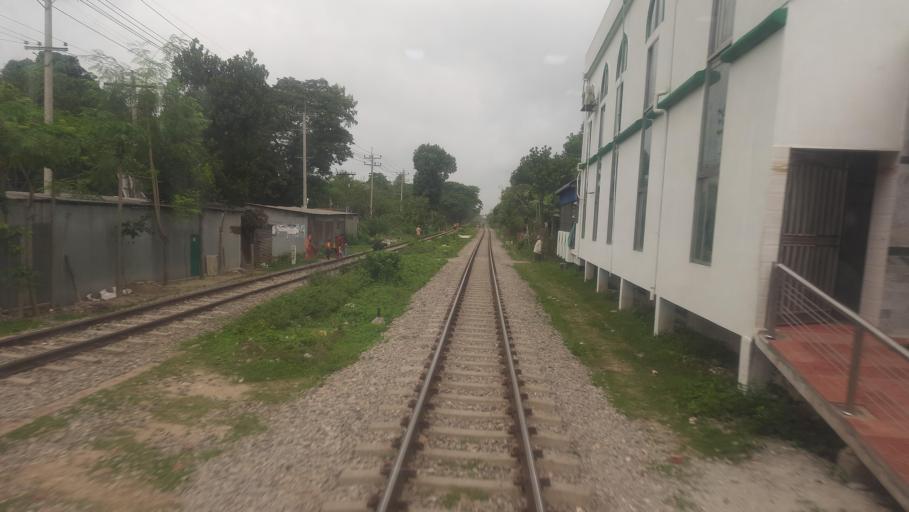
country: BD
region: Dhaka
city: Narsingdi
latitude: 23.9314
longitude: 90.7298
